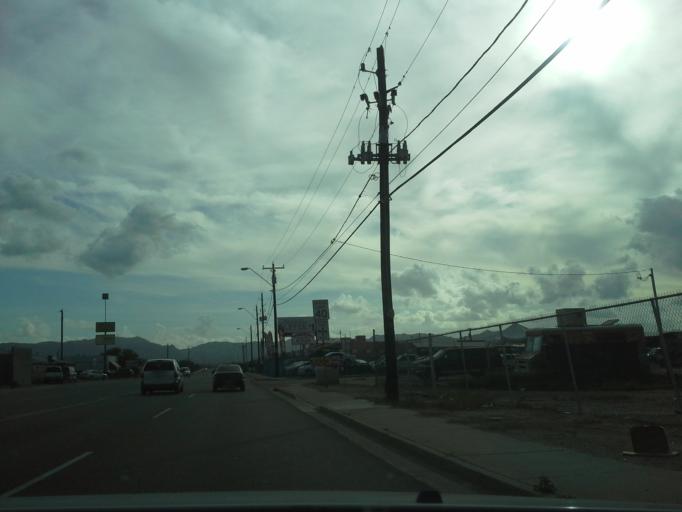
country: US
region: Arizona
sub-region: Maricopa County
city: Phoenix
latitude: 33.4250
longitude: -112.0825
